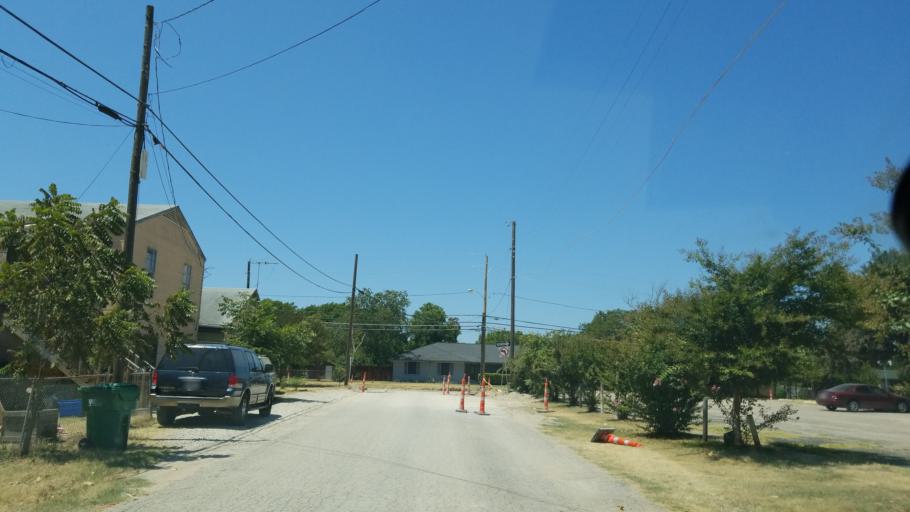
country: US
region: Texas
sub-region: Dallas County
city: Cockrell Hill
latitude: 32.7332
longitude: -96.8908
